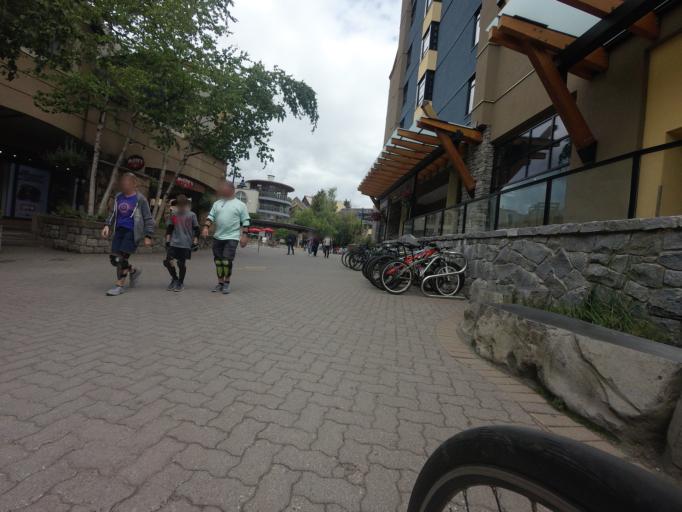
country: CA
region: British Columbia
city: Whistler
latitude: 50.1132
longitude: -122.9548
